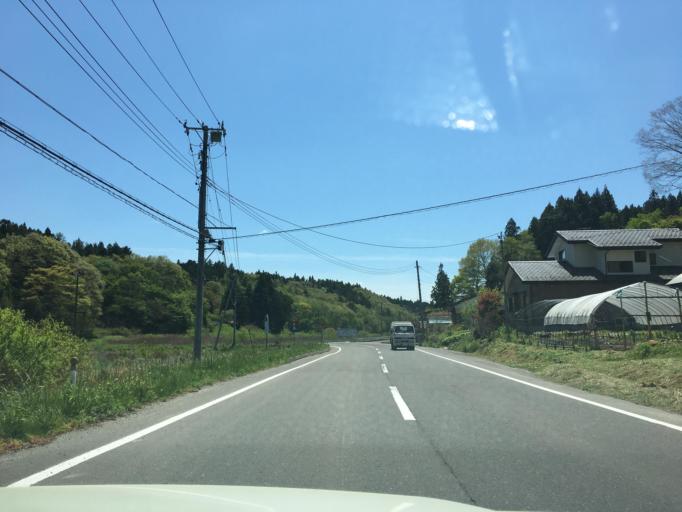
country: JP
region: Fukushima
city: Funehikimachi-funehiki
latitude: 37.3171
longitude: 140.6223
